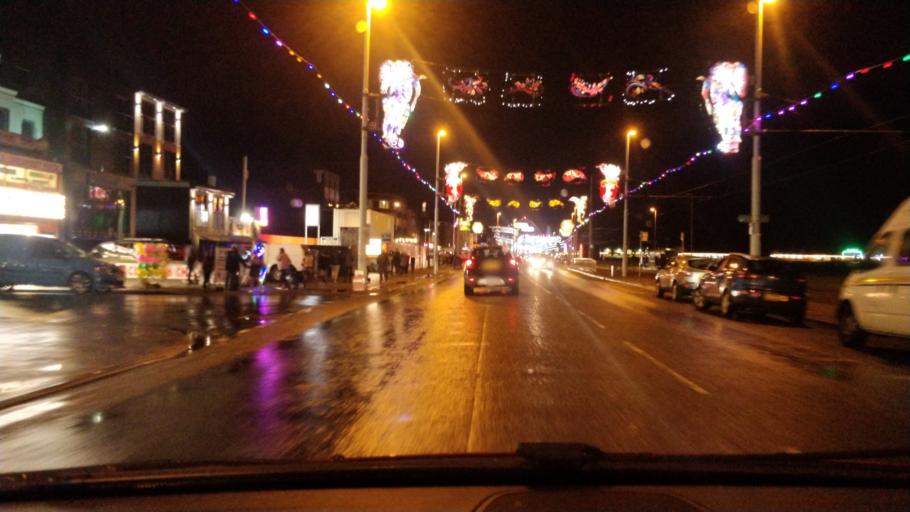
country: GB
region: England
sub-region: Blackpool
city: Blackpool
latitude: 53.7997
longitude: -3.0556
